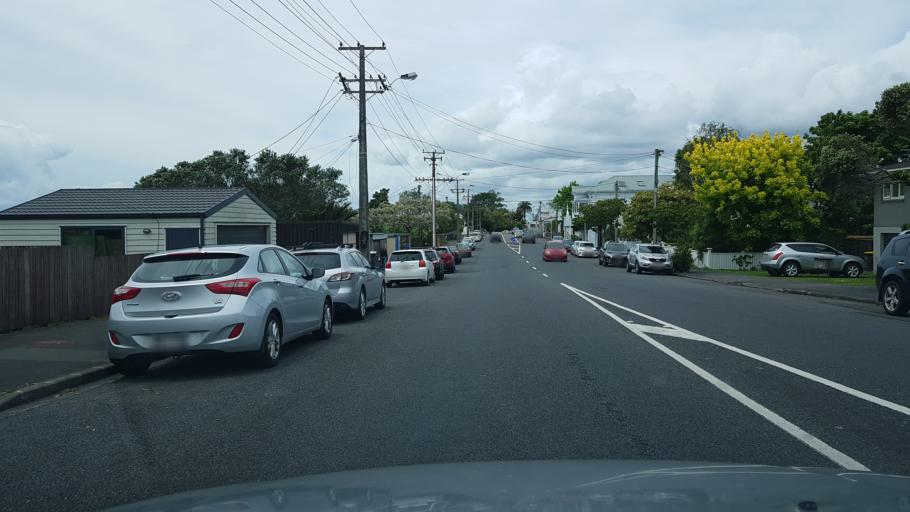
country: NZ
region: Auckland
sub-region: Auckland
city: North Shore
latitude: -36.8146
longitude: 174.7297
